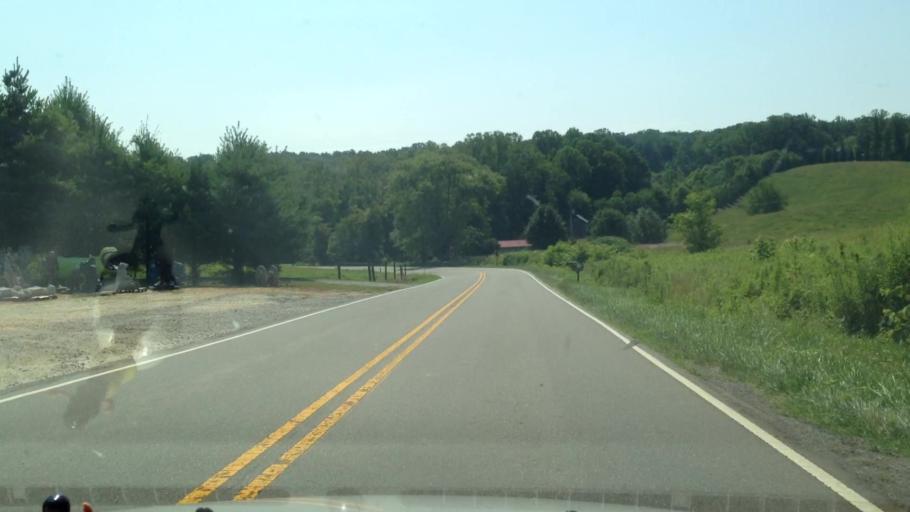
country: US
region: North Carolina
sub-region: Surry County
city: Flat Rock
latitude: 36.5347
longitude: -80.5118
